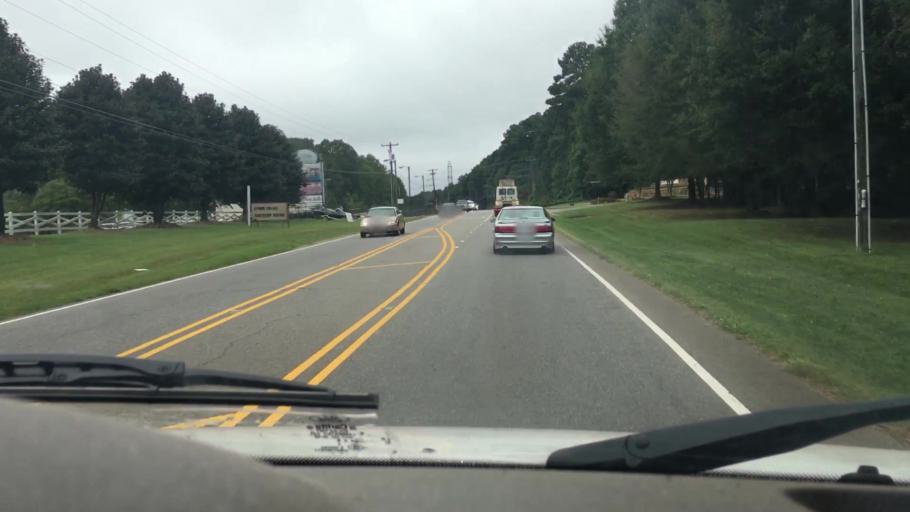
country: US
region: North Carolina
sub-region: Catawba County
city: Lake Norman of Catawba
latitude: 35.6048
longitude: -80.9294
